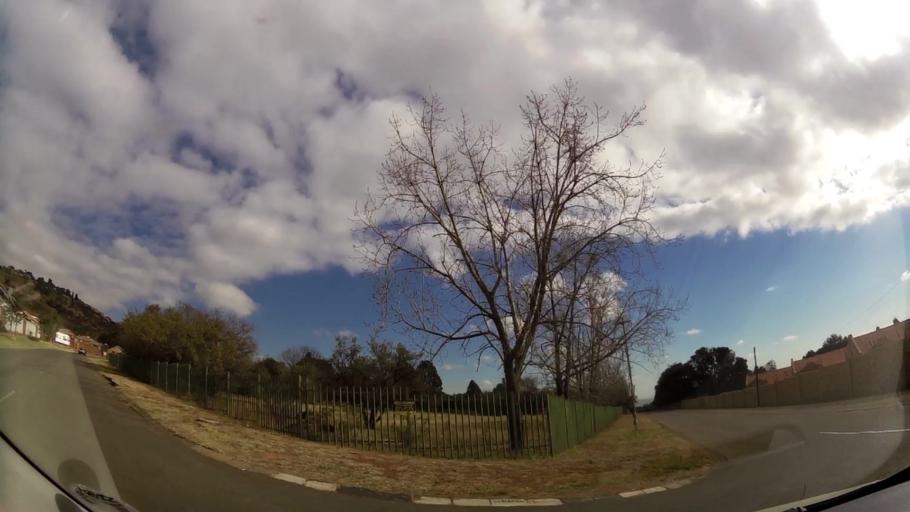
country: ZA
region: Gauteng
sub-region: City of Johannesburg Metropolitan Municipality
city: Roodepoort
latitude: -26.1033
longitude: 27.8722
